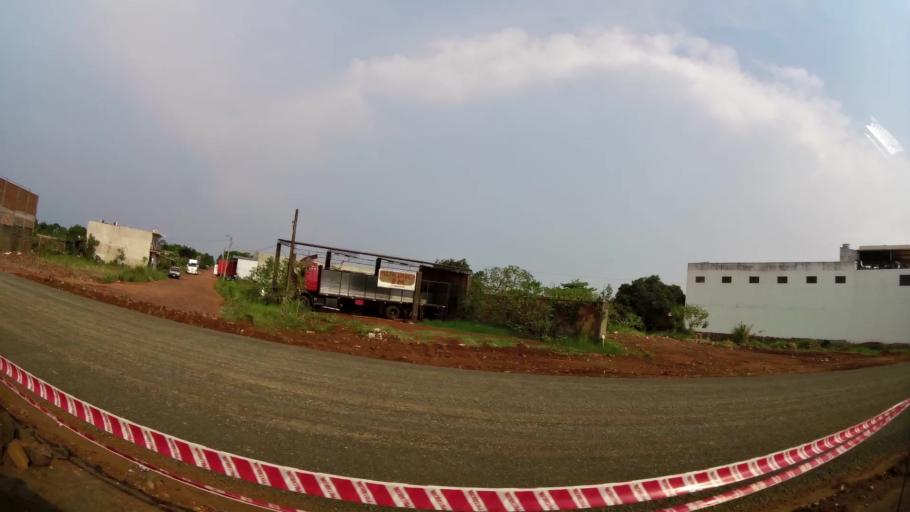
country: PY
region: Alto Parana
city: Ciudad del Este
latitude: -25.4777
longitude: -54.6542
